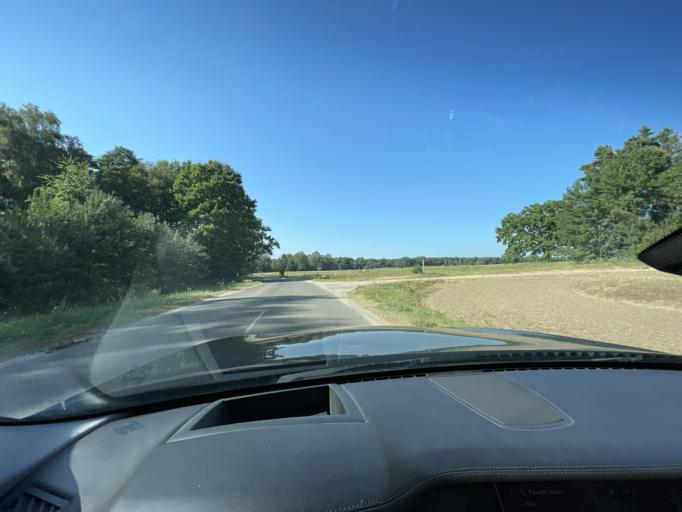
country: BY
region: Grodnenskaya
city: Hrodna
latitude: 53.7589
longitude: 23.9663
